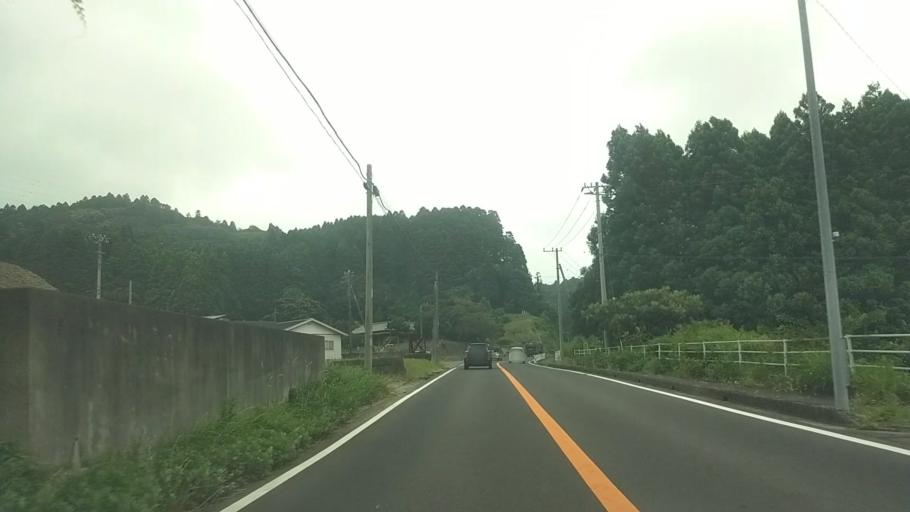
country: JP
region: Chiba
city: Ohara
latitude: 35.2655
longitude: 140.3628
